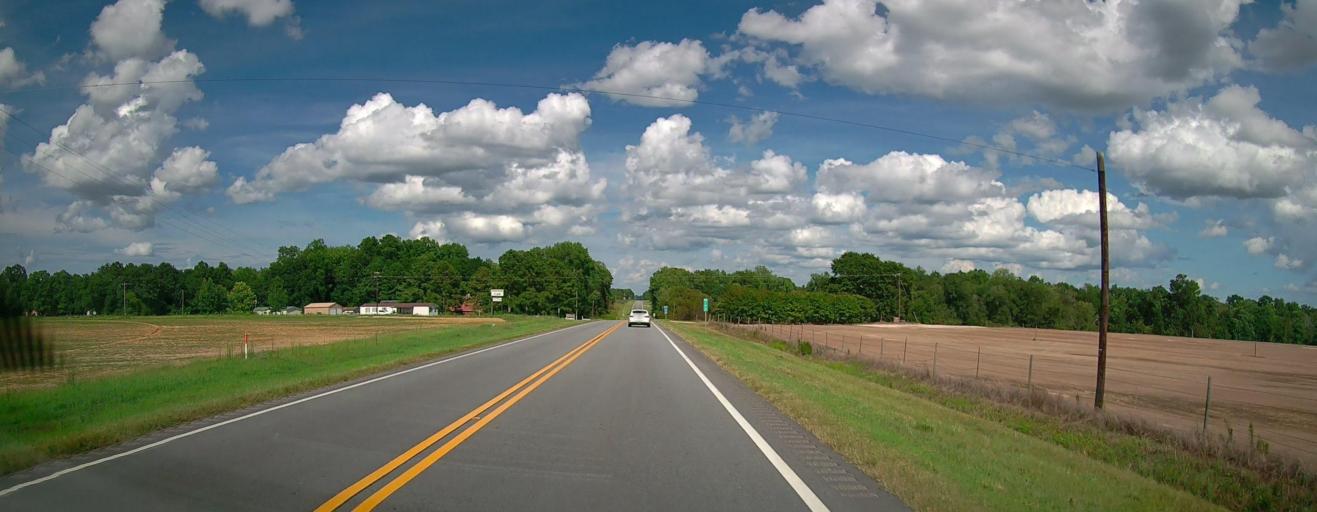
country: US
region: Alabama
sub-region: Lee County
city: Auburn
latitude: 32.4352
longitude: -85.4076
